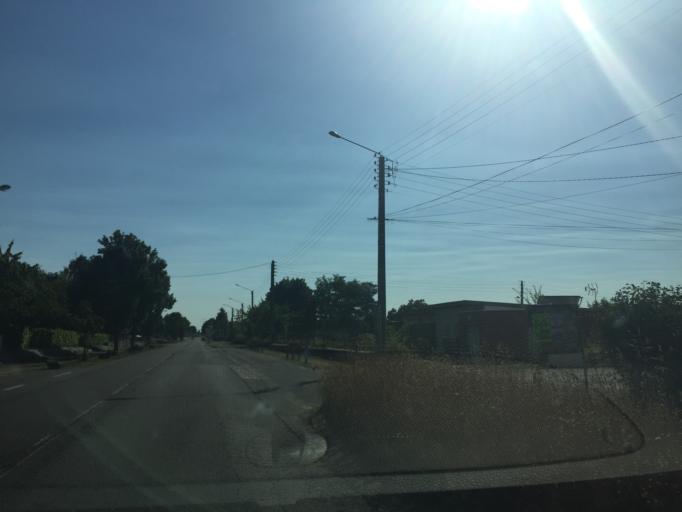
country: FR
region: Poitou-Charentes
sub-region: Departement des Deux-Sevres
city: Melle
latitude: 46.2231
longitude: -0.1323
